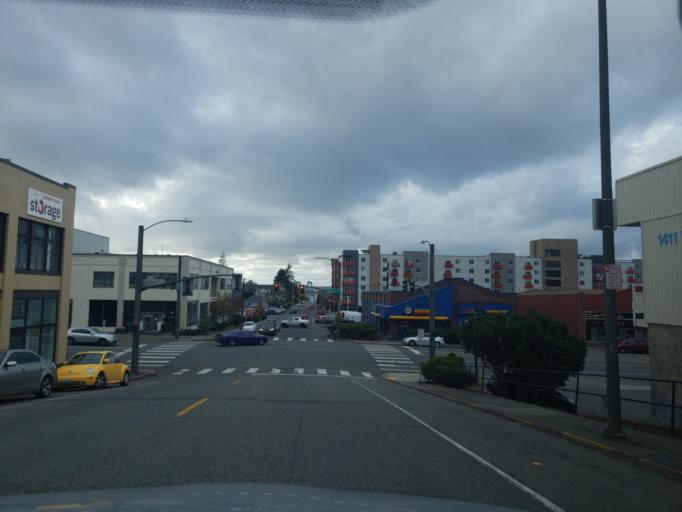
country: US
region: Washington
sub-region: Snohomish County
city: Everett
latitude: 47.9778
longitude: -122.2107
